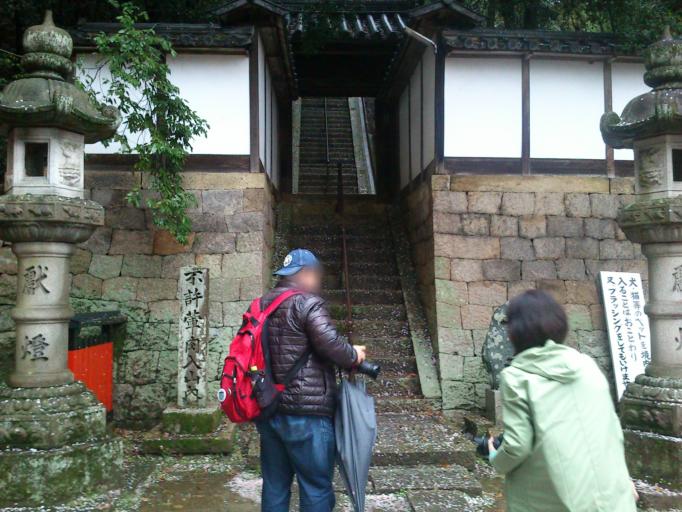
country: JP
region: Kyoto
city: Yawata
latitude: 34.8970
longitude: 135.6827
